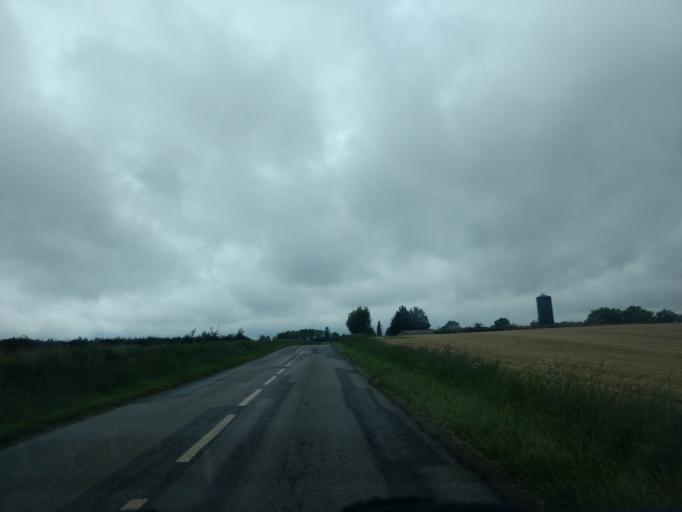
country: FR
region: Midi-Pyrenees
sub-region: Departement de l'Aveyron
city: Montbazens
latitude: 44.5110
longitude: 2.1894
